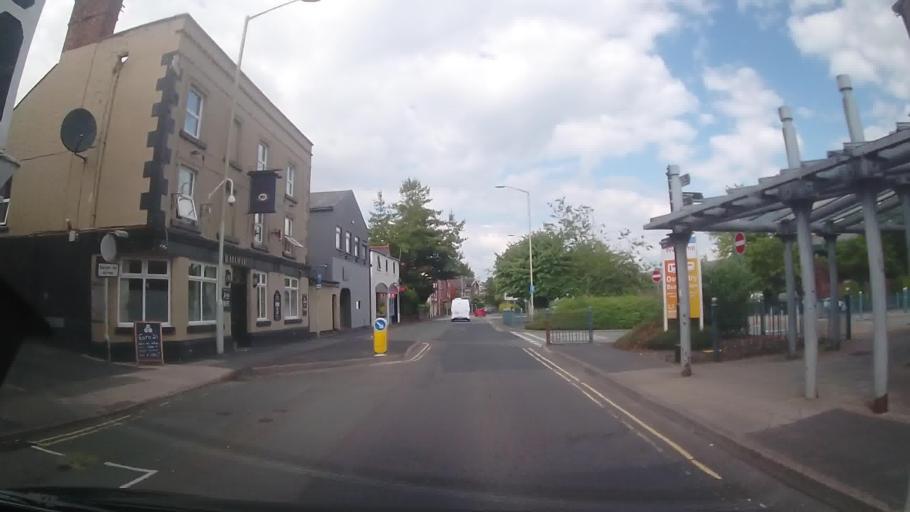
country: GB
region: England
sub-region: Shropshire
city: Oswestry
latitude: 52.8621
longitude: -3.0516
